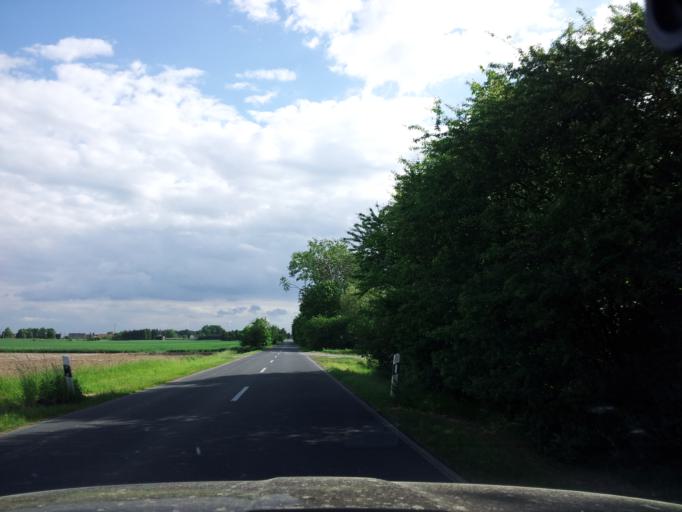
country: DE
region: Saxony-Anhalt
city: Seyda
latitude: 51.9635
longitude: 12.9003
